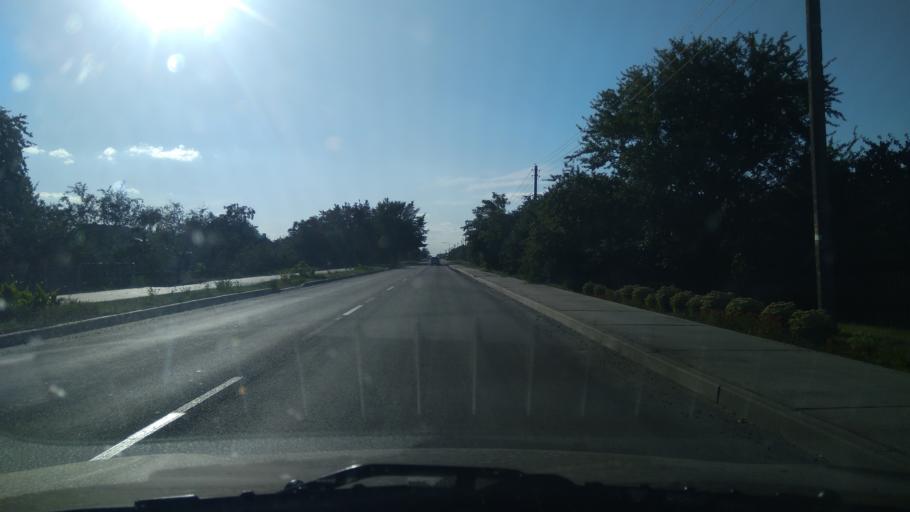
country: BY
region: Brest
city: Byaroza
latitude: 52.5422
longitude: 24.9720
